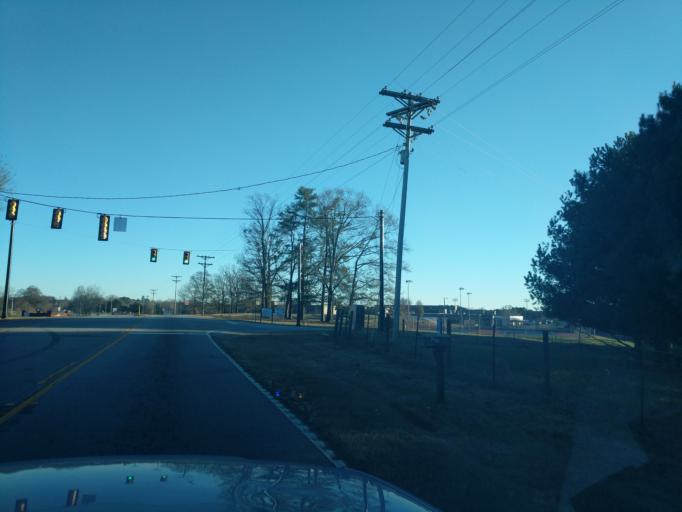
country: US
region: South Carolina
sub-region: Oconee County
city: Westminster
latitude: 34.6248
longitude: -83.0543
